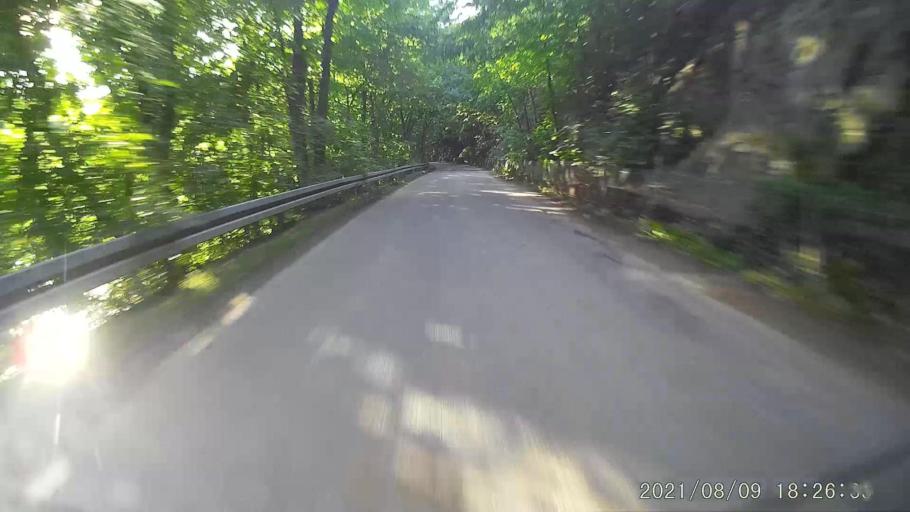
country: PL
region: Lower Silesian Voivodeship
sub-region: Powiat zabkowicki
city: Bardo
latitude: 50.5100
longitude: 16.7352
